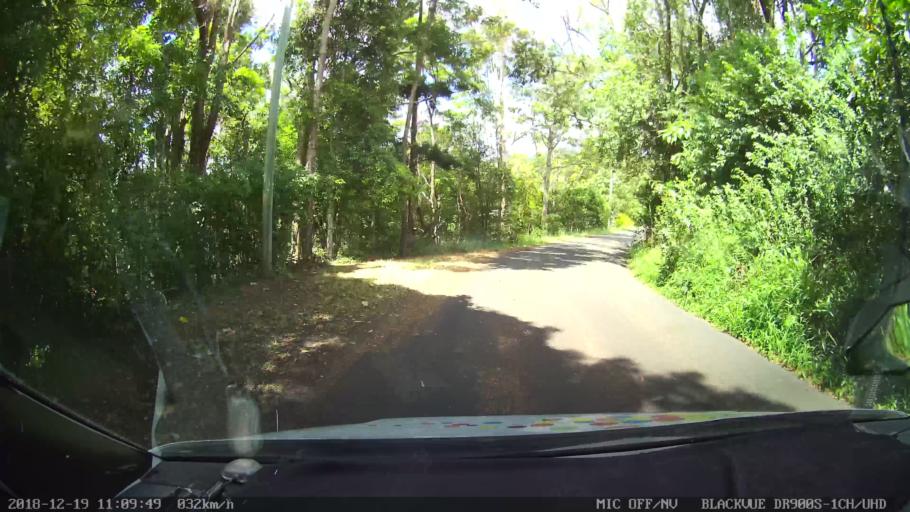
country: AU
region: New South Wales
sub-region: Lismore Municipality
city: Nimbin
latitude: -28.6352
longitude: 153.2629
